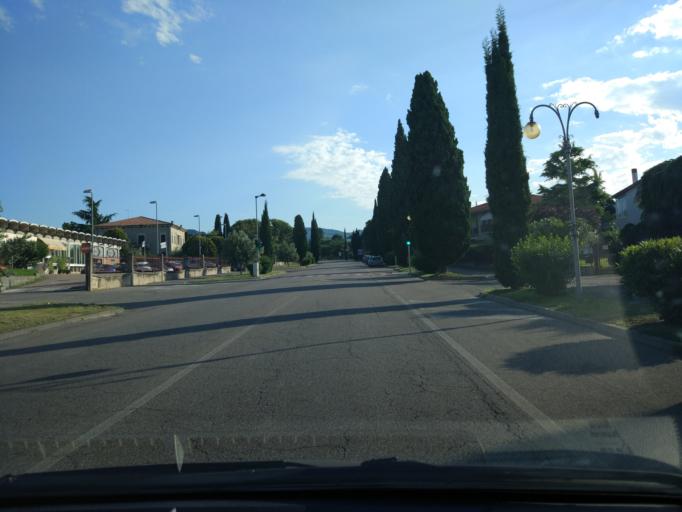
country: IT
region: Veneto
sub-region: Provincia di Verona
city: Illasi
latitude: 45.4630
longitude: 11.1781
